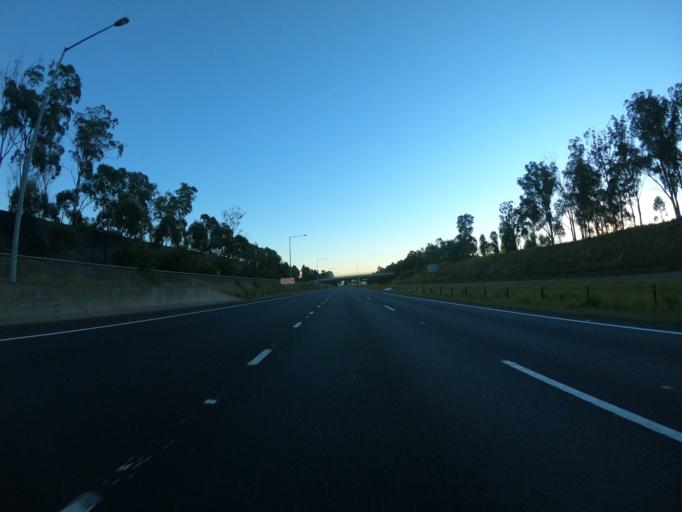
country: AU
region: New South Wales
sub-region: Blacktown
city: Glendenning
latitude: -33.7473
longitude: 150.8460
